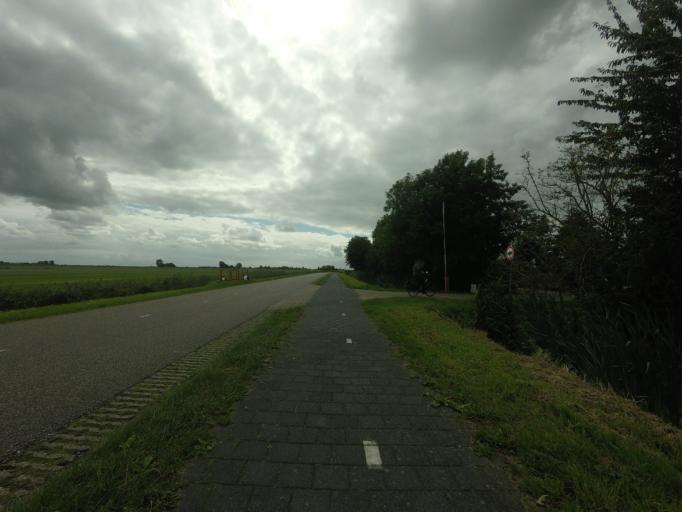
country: NL
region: Friesland
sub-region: Sudwest Fryslan
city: Heeg
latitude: 52.9904
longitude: 5.5446
